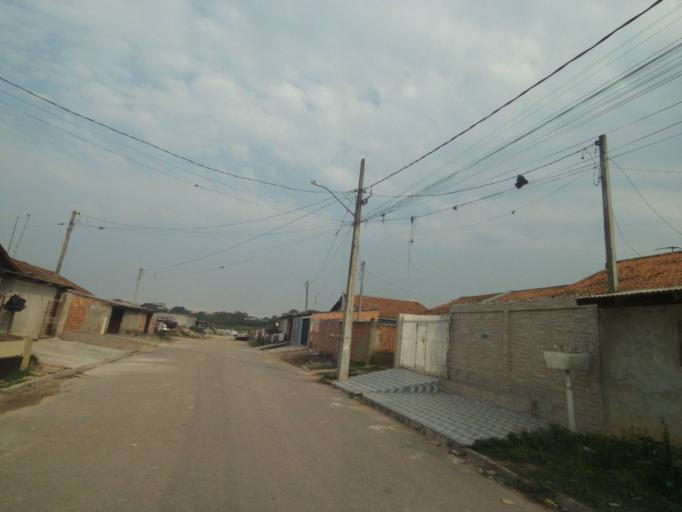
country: BR
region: Parana
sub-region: Sao Jose Dos Pinhais
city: Sao Jose dos Pinhais
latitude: -25.5333
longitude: -49.2300
